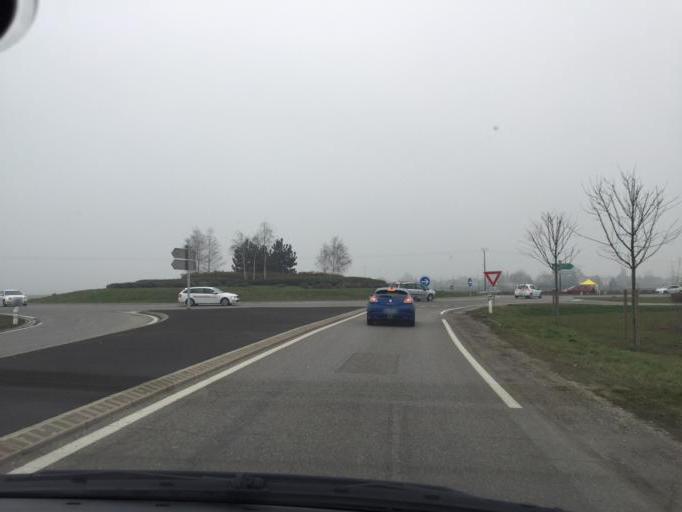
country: FR
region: Alsace
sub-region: Departement du Haut-Rhin
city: Andolsheim
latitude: 48.0726
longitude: 7.4088
